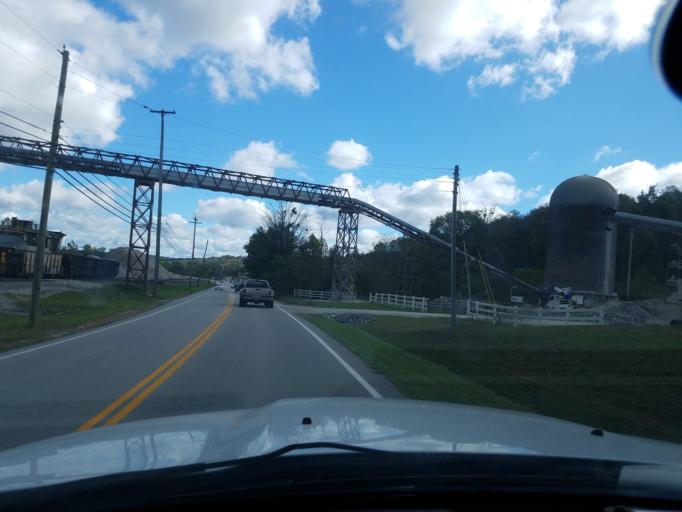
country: US
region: Kentucky
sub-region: Rockcastle County
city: Mount Vernon
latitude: 37.3503
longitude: -84.3513
